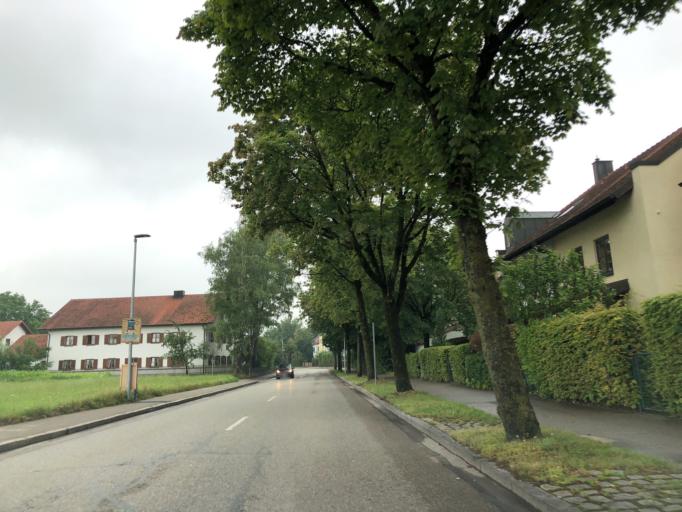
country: DE
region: Bavaria
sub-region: Upper Bavaria
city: Erding
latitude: 48.2963
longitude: 11.9096
